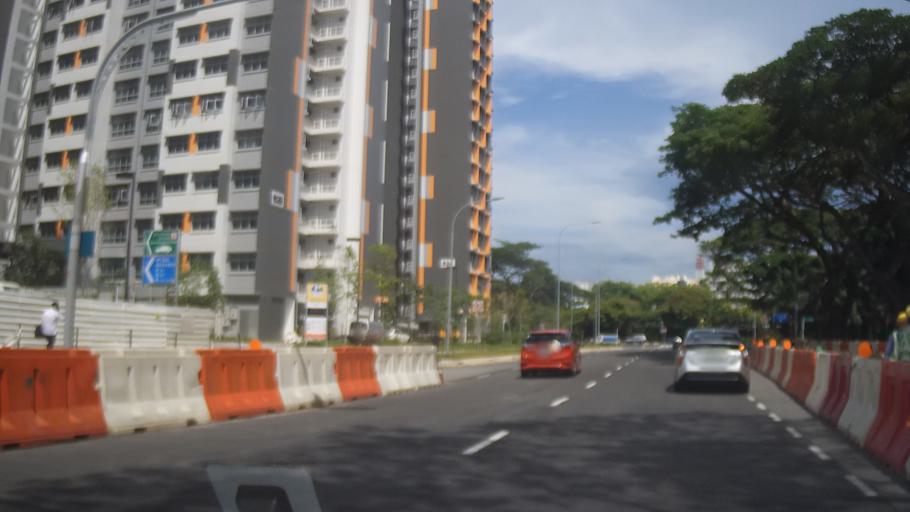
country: SG
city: Singapore
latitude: 1.3241
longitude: 103.8888
